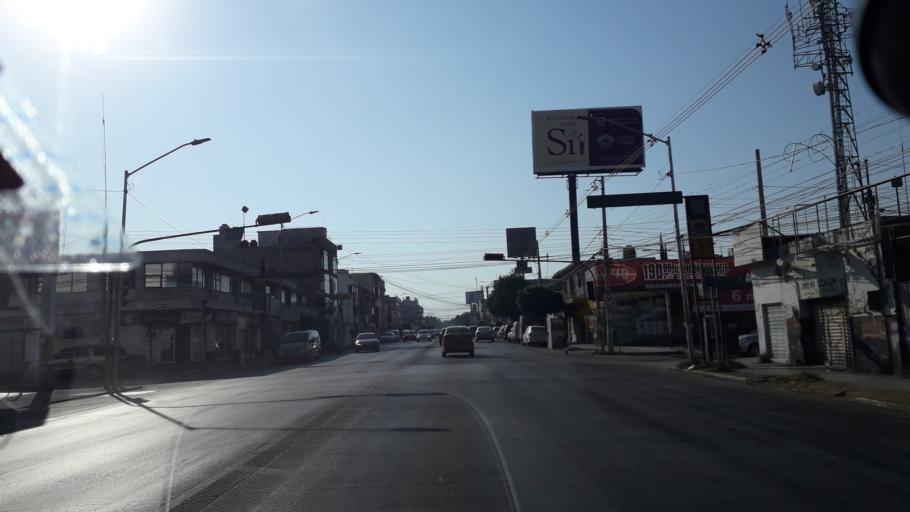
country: MX
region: Puebla
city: Puebla
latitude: 19.0427
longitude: -98.2252
